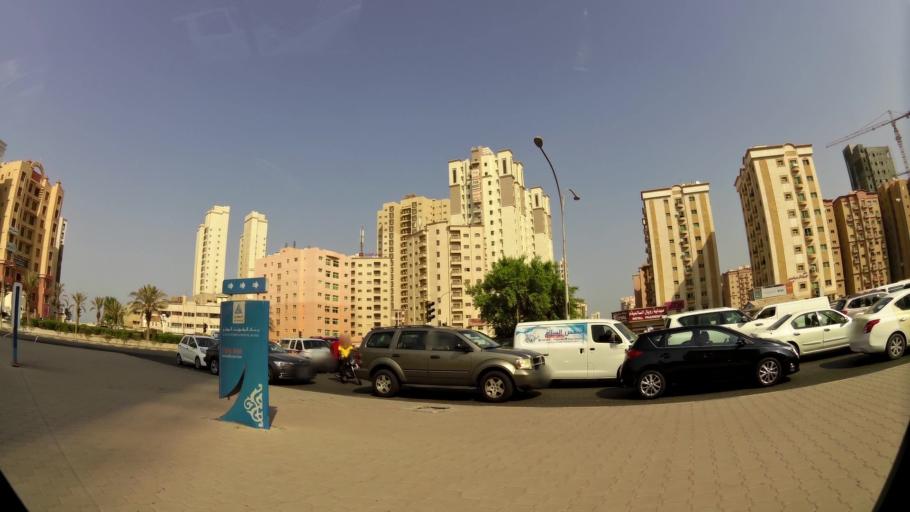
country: KW
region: Muhafazat Hawalli
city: As Salimiyah
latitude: 29.3361
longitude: 48.0535
